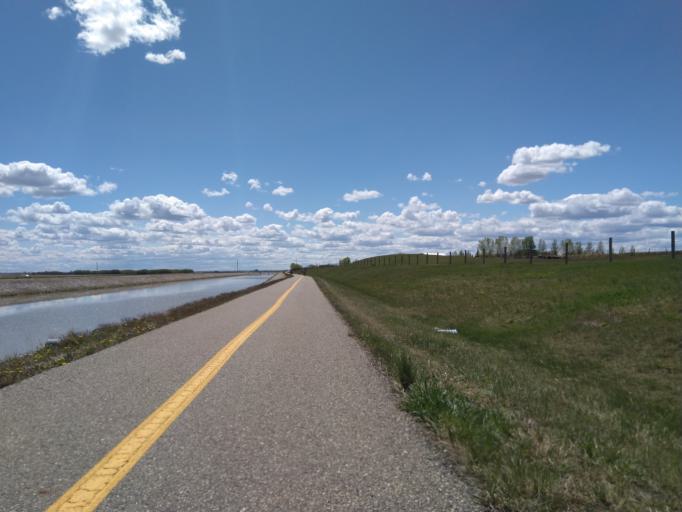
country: CA
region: Alberta
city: Chestermere
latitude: 51.0147
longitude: -113.8441
